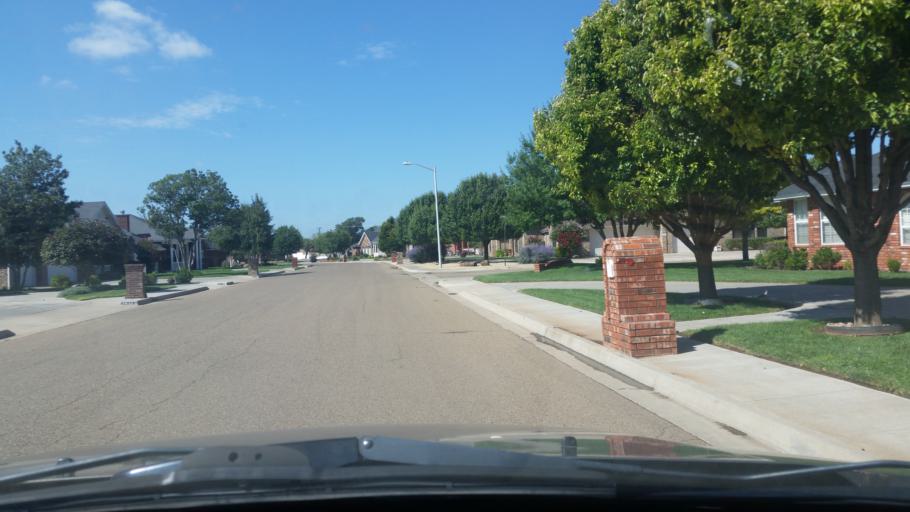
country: US
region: New Mexico
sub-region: Curry County
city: Clovis
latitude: 34.4404
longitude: -103.1768
